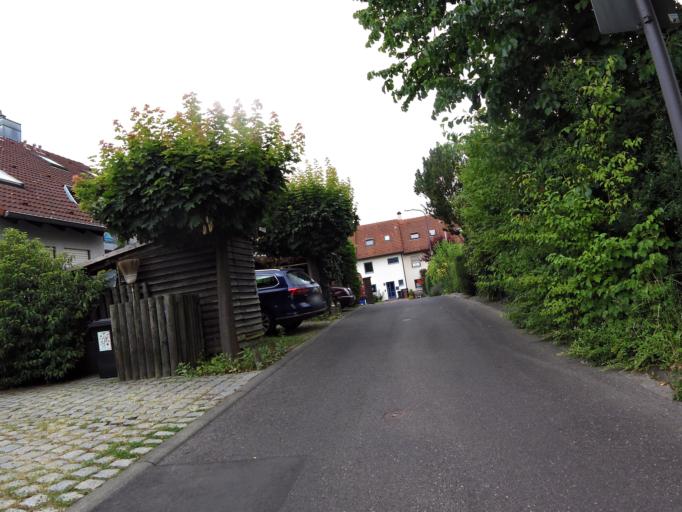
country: DE
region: Bavaria
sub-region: Regierungsbezirk Unterfranken
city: Wuerzburg
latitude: 49.7608
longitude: 9.9398
